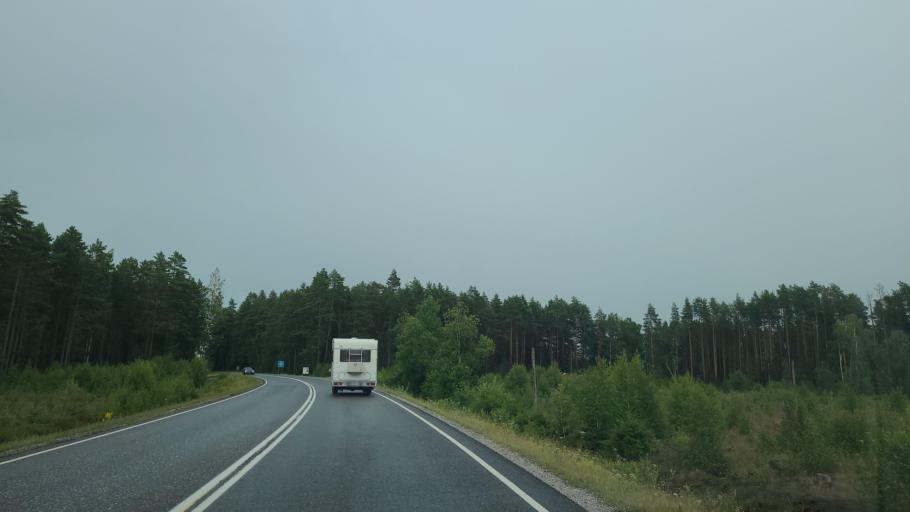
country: FI
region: Varsinais-Suomi
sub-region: Turku
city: Sauvo
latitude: 60.3186
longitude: 22.7052
